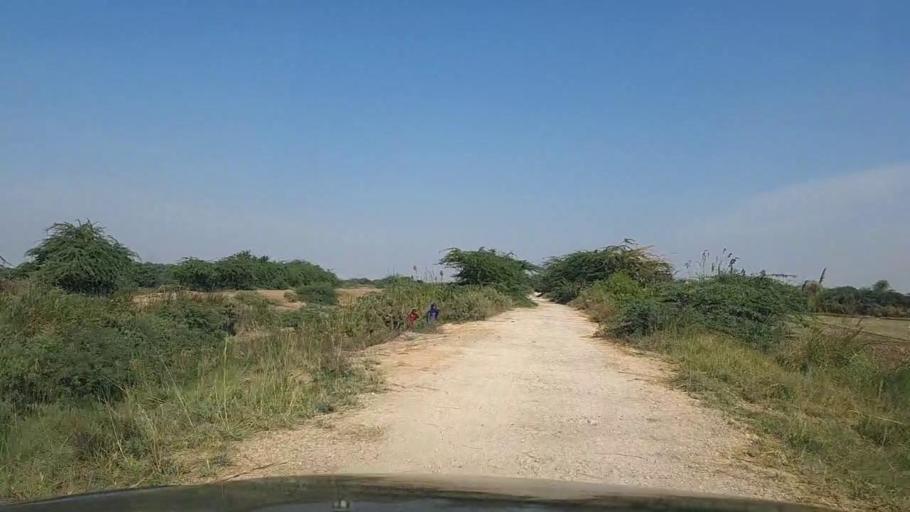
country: PK
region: Sindh
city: Thatta
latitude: 24.7133
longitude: 67.7933
